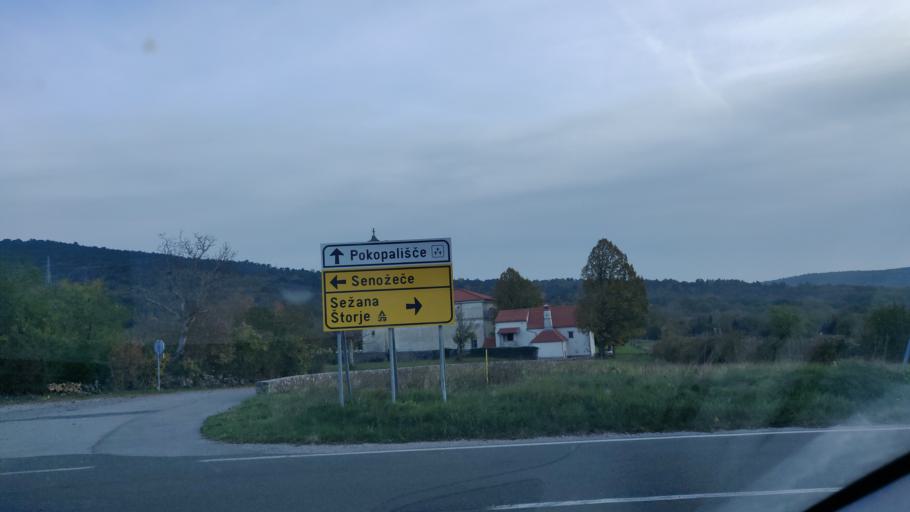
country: SI
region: Sezana
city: Sezana
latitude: 45.7397
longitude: 13.9326
